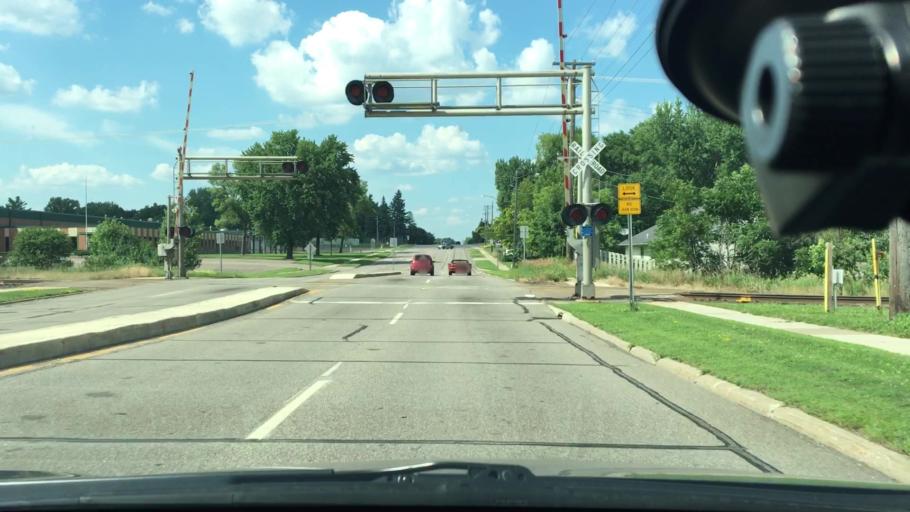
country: US
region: Minnesota
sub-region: Hennepin County
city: New Hope
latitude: 45.0483
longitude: -93.3803
